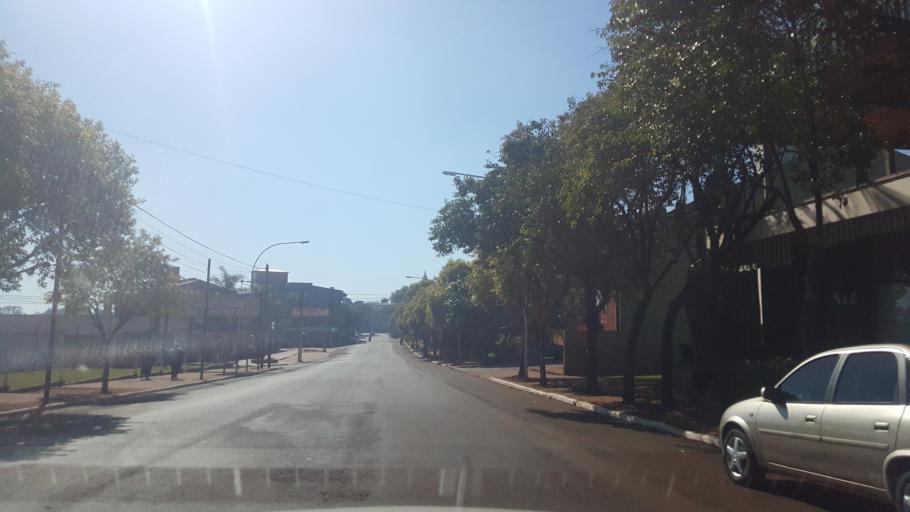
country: AR
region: Misiones
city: Puerto Rico
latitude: -26.8215
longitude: -55.0285
